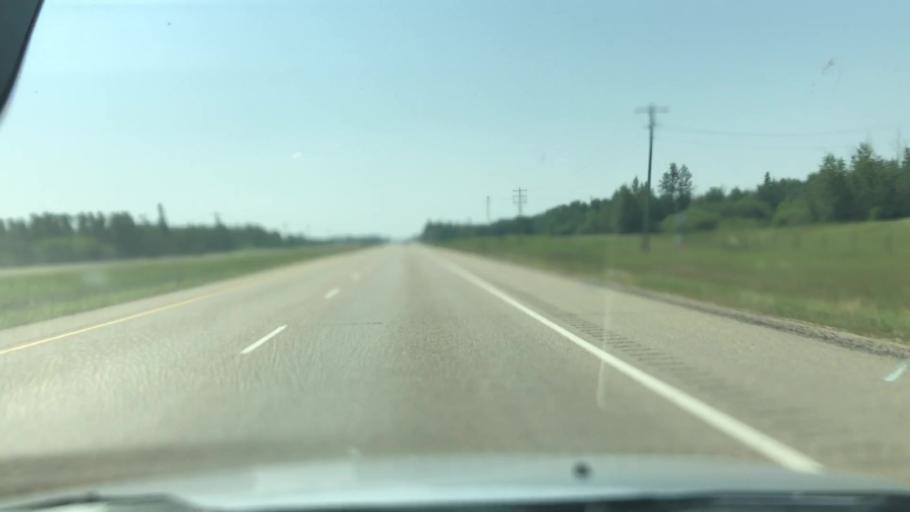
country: CA
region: Alberta
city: Devon
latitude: 53.4396
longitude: -113.7631
